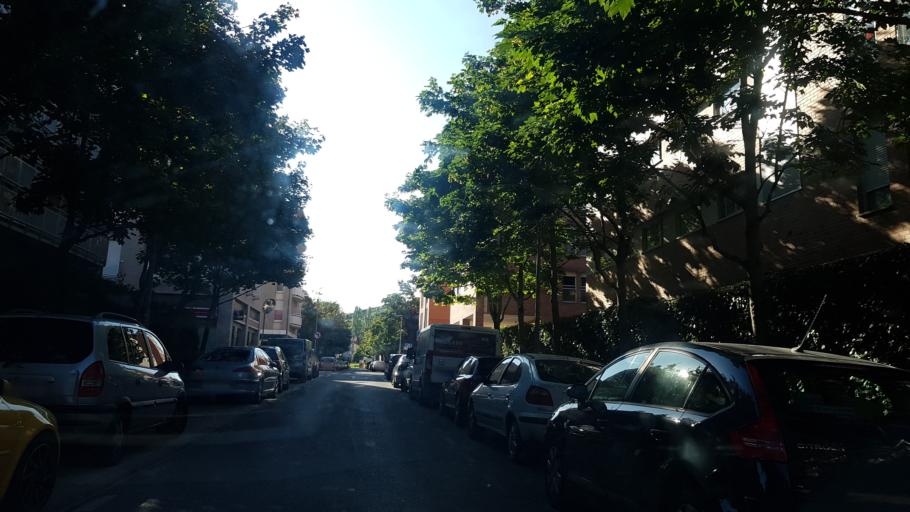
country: ES
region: Navarre
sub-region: Provincia de Navarra
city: Burlata
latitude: 42.8119
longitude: -1.6135
